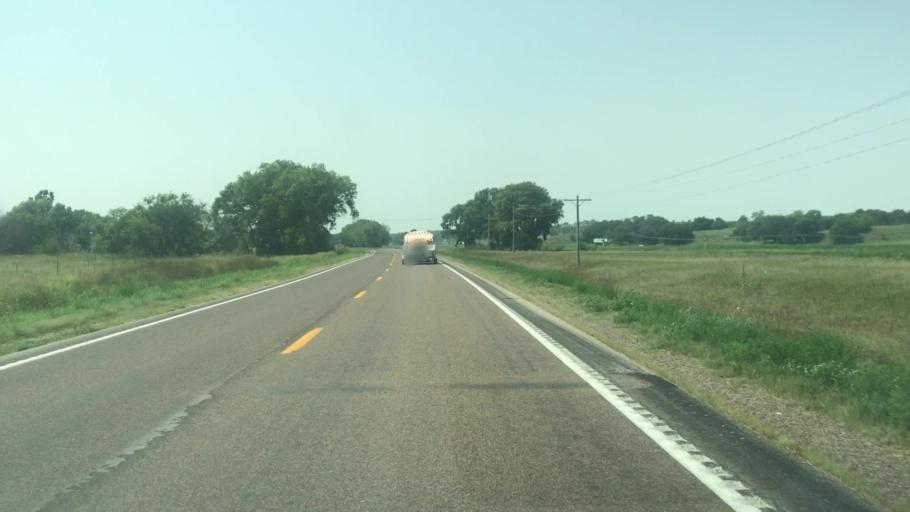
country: US
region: Nebraska
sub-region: Buffalo County
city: Ravenna
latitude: 41.0768
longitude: -98.6935
